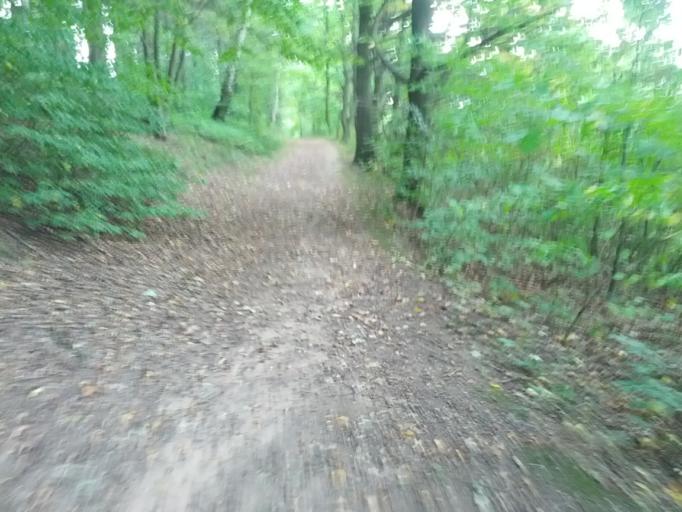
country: DE
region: Thuringia
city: Thal
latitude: 50.9444
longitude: 10.3991
